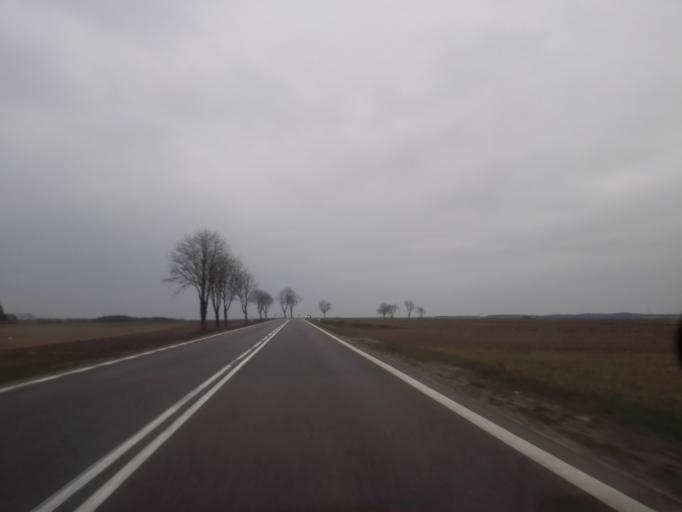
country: PL
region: Podlasie
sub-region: Powiat grajewski
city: Szczuczyn
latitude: 53.5752
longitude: 22.3119
